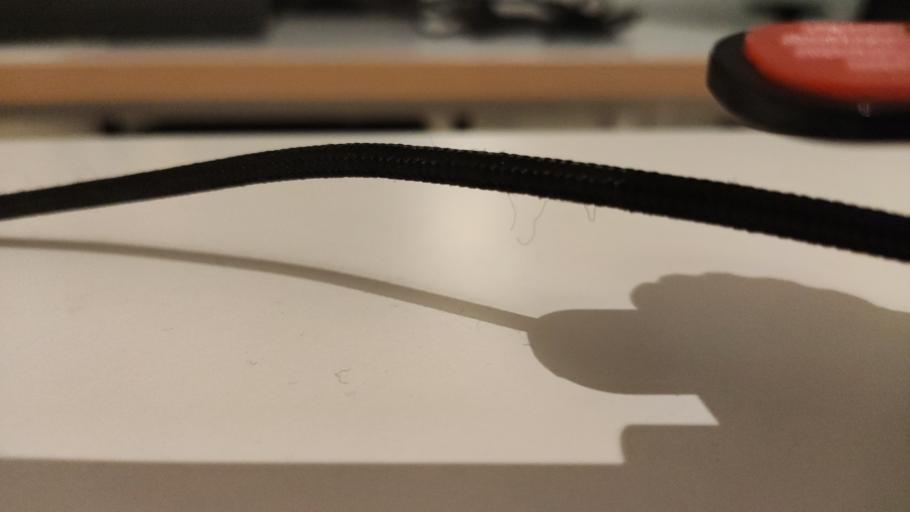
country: RU
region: Moskovskaya
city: Meshcherino
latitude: 55.2321
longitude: 38.4146
